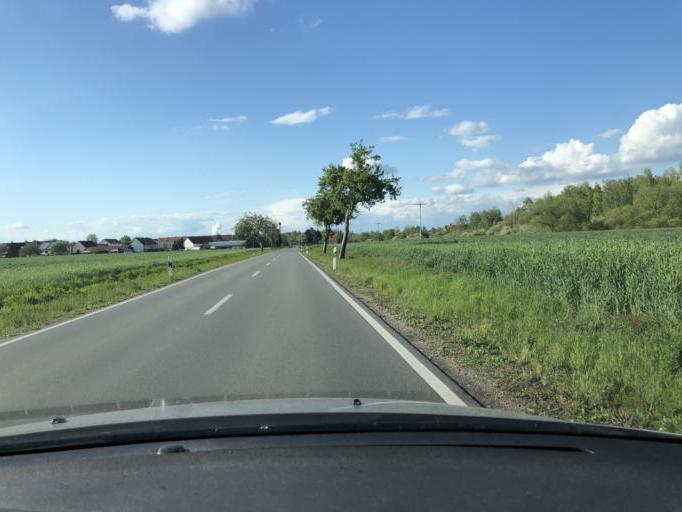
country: DE
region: Saxony
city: Regis-Breitingen
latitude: 51.1039
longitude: 12.4301
